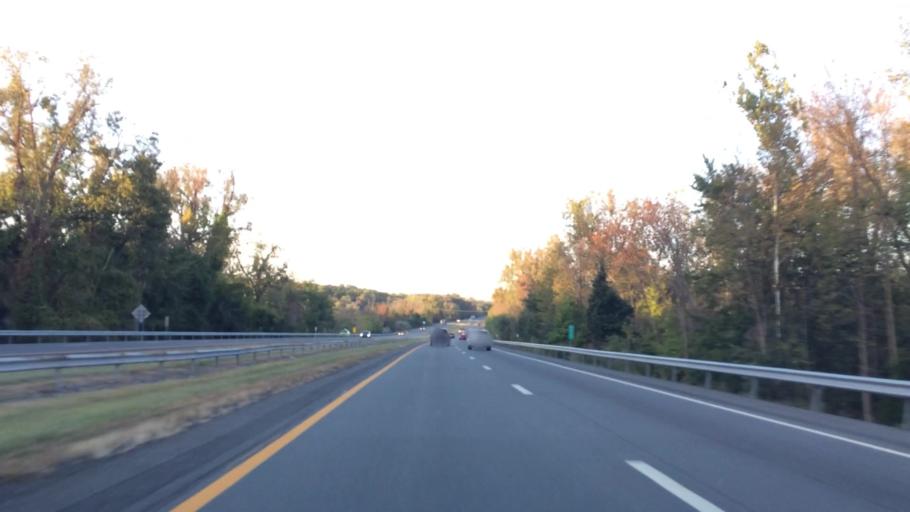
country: US
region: New York
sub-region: Orange County
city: Vails Gate
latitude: 41.4383
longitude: -74.0672
